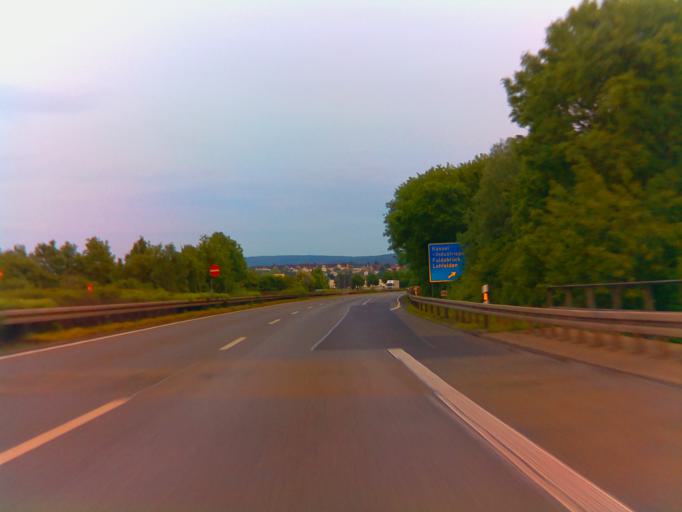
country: DE
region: Hesse
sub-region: Regierungsbezirk Kassel
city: Lohfelden
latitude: 51.2850
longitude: 9.5170
